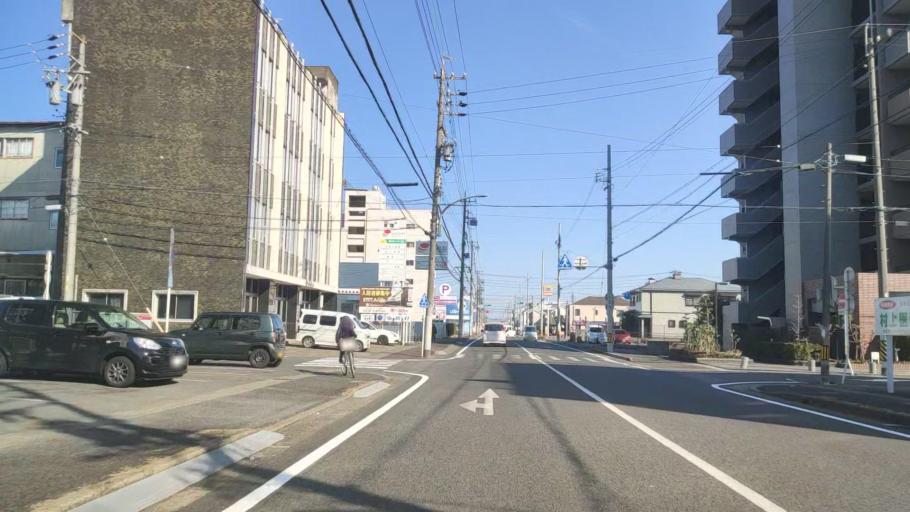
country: JP
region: Gifu
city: Gifu-shi
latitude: 35.4147
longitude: 136.7776
